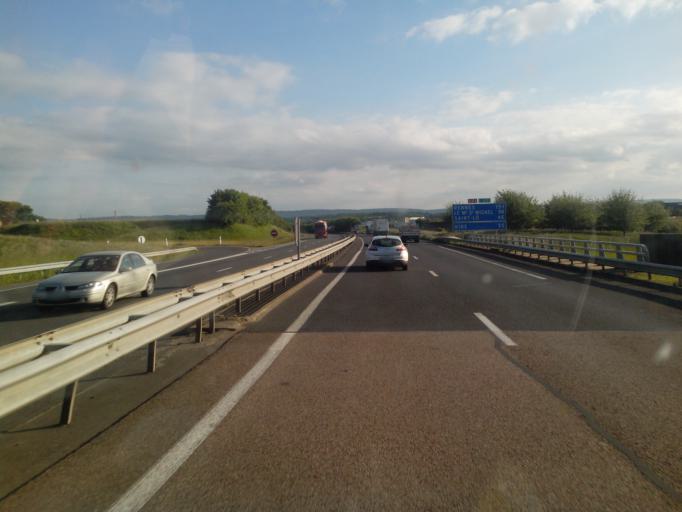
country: FR
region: Lower Normandy
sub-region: Departement du Calvados
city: Villers-Bocage
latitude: 49.0872
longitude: -0.6366
